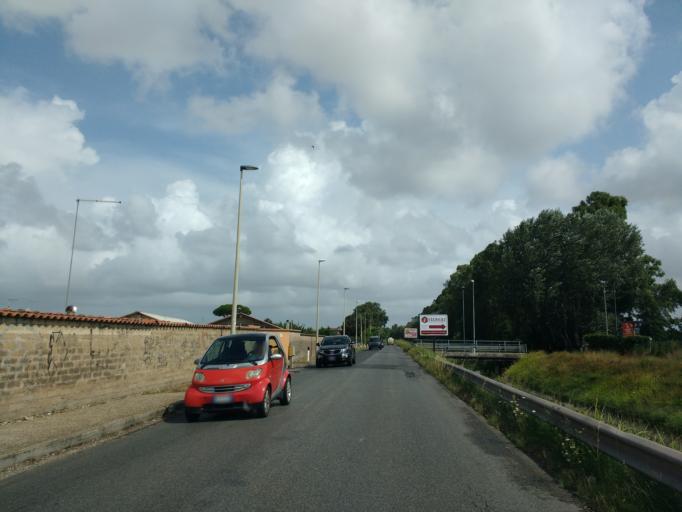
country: IT
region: Latium
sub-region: Citta metropolitana di Roma Capitale
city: Acilia-Castel Fusano-Ostia Antica
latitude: 41.7536
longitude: 12.3300
